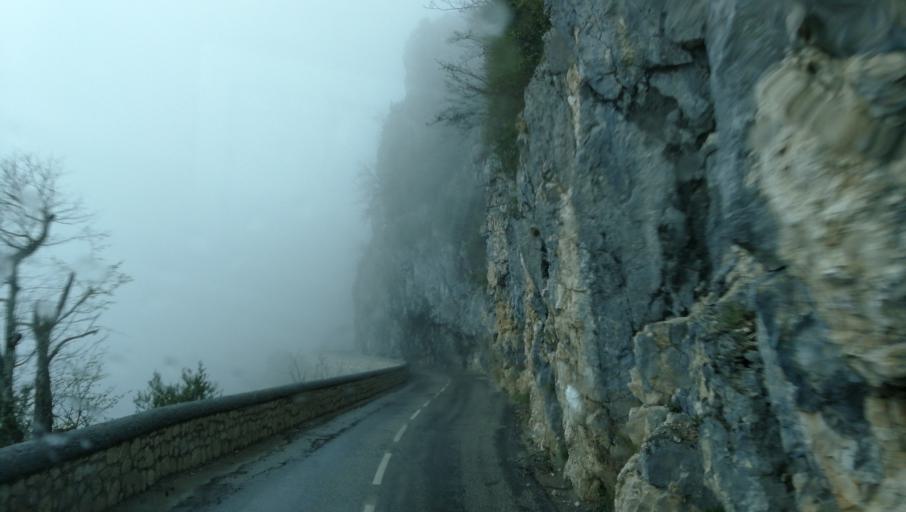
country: FR
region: Rhone-Alpes
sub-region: Departement de la Drome
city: Saint-Laurent-en-Royans
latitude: 44.9813
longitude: 5.3332
